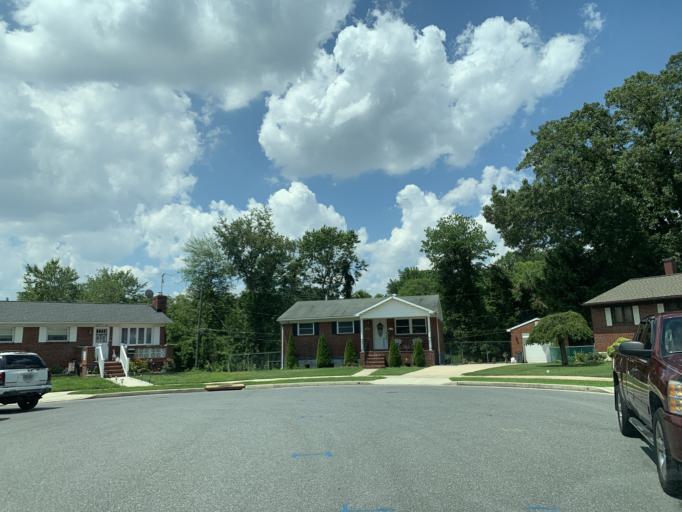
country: US
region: Maryland
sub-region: Baltimore County
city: Essex
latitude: 39.3083
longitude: -76.4673
